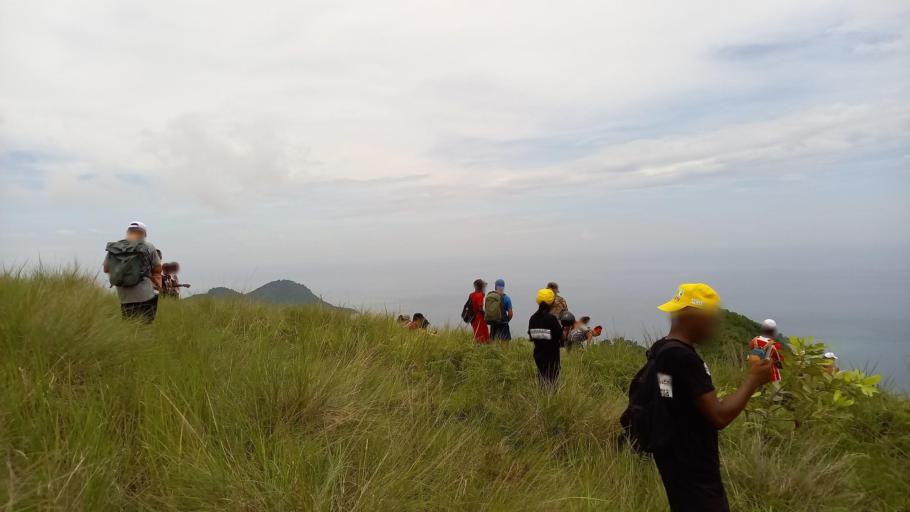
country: YT
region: Acoua
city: Acoua
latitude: -12.7121
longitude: 45.0593
